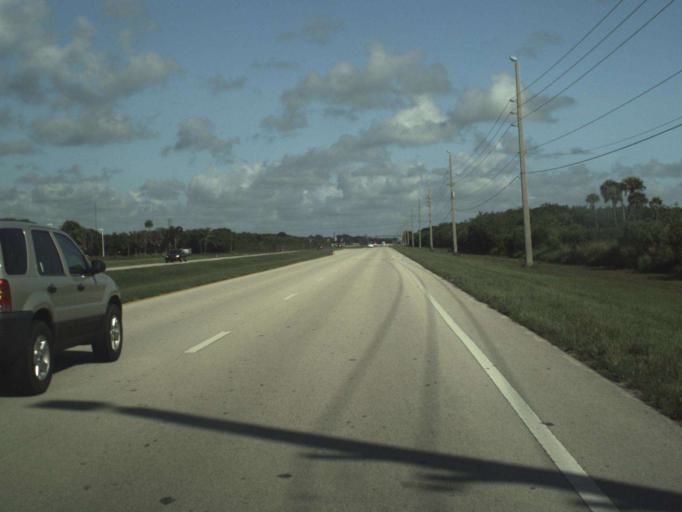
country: US
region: Florida
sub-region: Indian River County
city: Gifford
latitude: 27.6625
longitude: -80.3881
